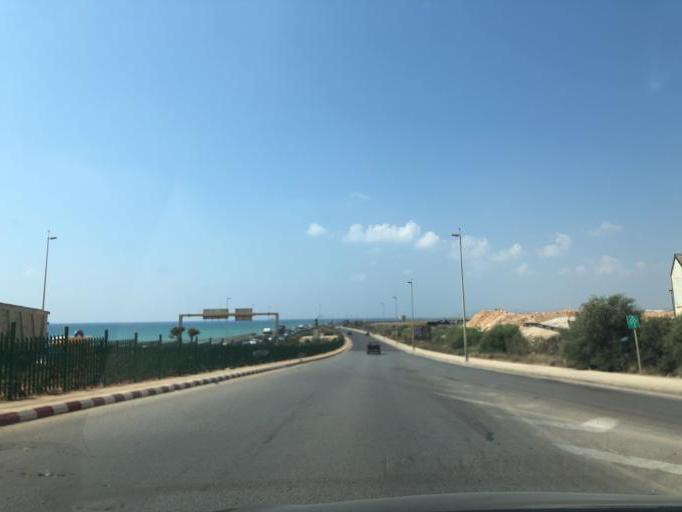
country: LB
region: Mont-Liban
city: Baabda
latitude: 33.7915
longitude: 35.4797
